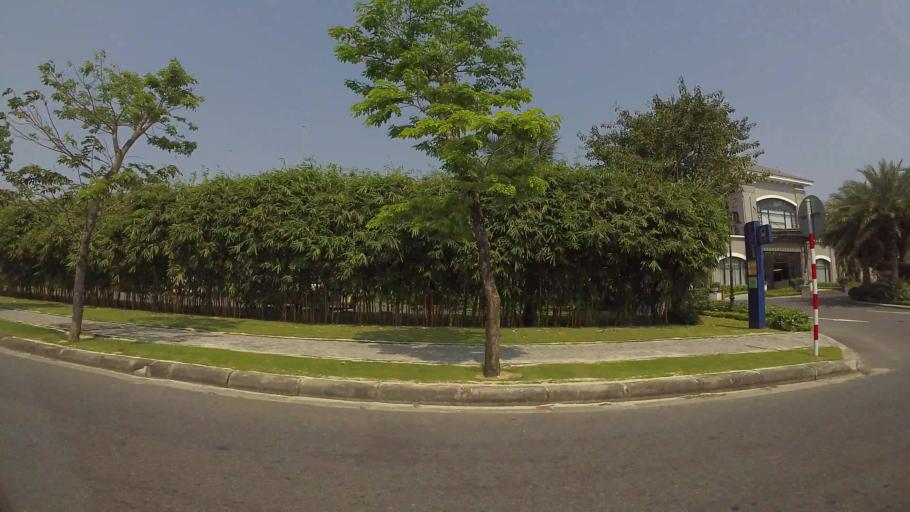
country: VN
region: Da Nang
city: Ngu Hanh Son
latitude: 15.9943
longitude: 108.2685
